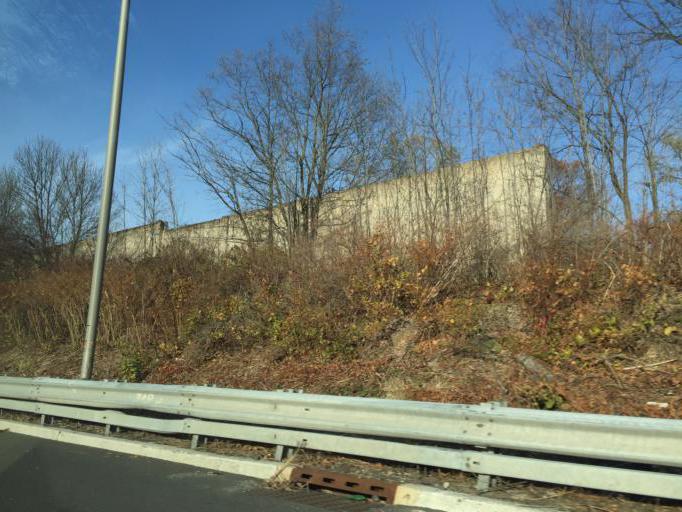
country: US
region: New Jersey
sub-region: Union County
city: Springfield
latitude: 40.7143
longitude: -74.3255
